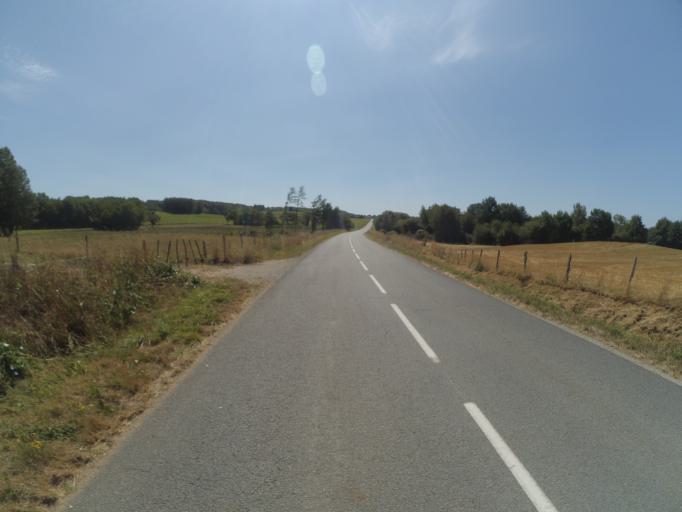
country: FR
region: Limousin
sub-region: Departement de la Creuse
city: Le Grand-Bourg
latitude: 46.0927
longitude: 1.6838
